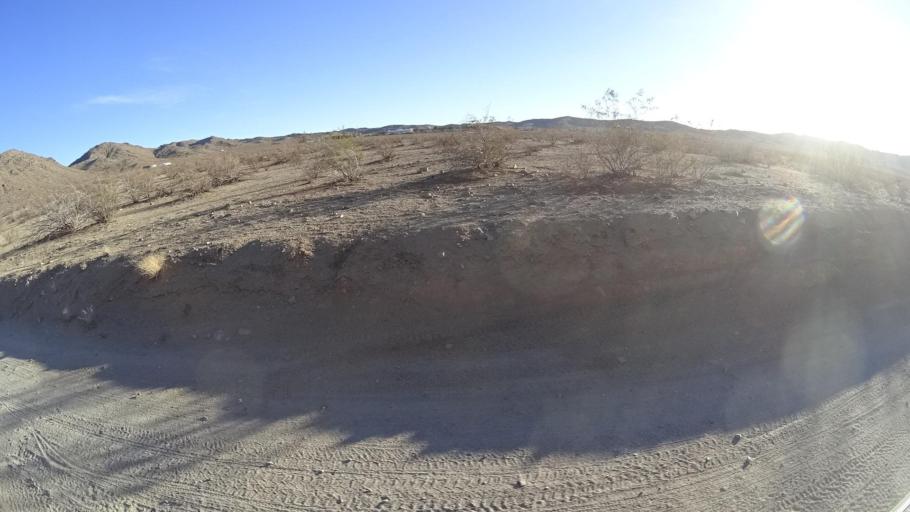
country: US
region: California
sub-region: Kern County
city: Ridgecrest
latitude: 35.5788
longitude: -117.6683
